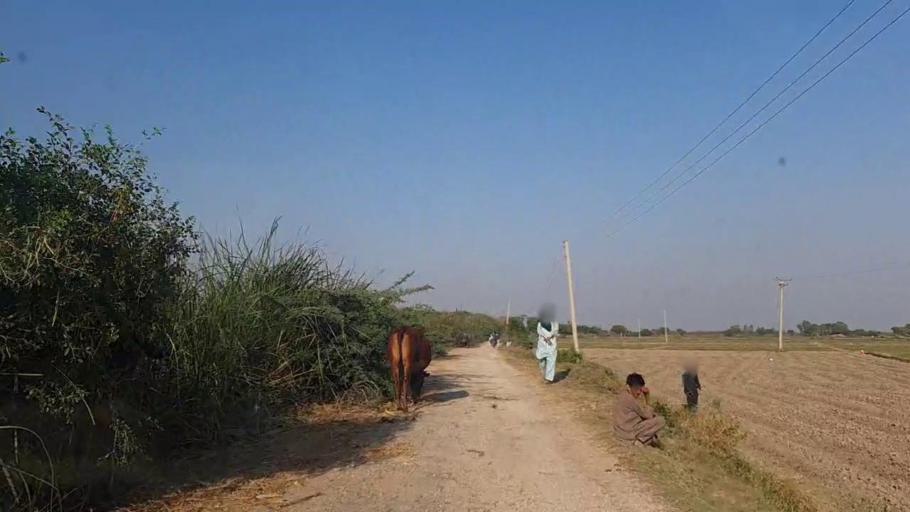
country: PK
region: Sindh
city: Thatta
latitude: 24.7190
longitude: 67.9432
